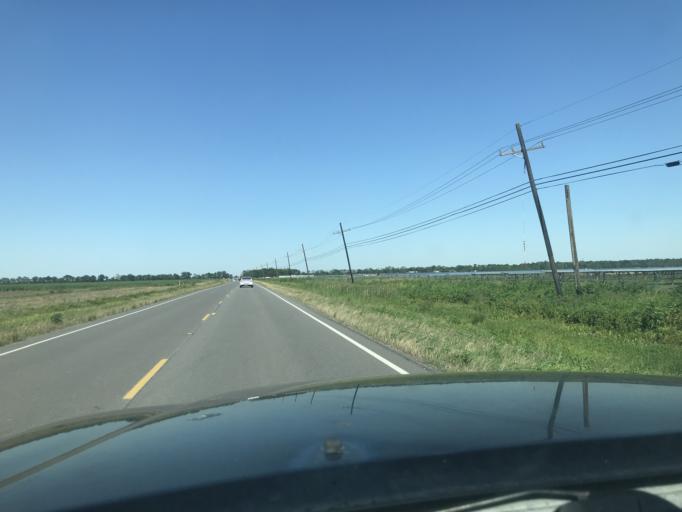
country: US
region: Louisiana
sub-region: West Baton Rouge Parish
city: Erwinville
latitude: 30.4686
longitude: -91.3382
